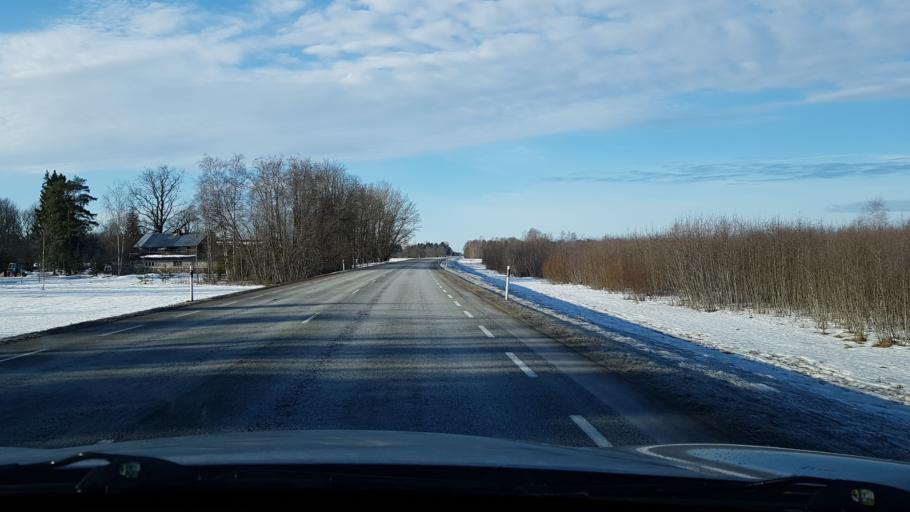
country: EE
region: Viljandimaa
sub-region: Vohma linn
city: Vohma
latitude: 58.6727
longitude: 25.6575
